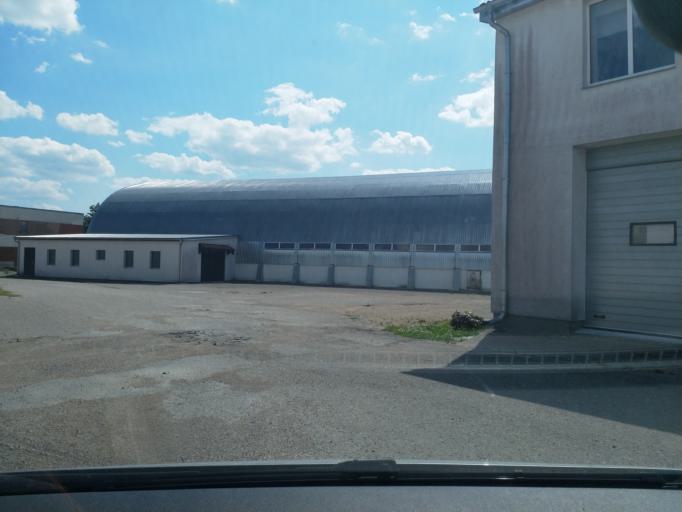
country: LV
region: Kuldigas Rajons
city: Kuldiga
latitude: 56.9661
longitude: 21.9251
